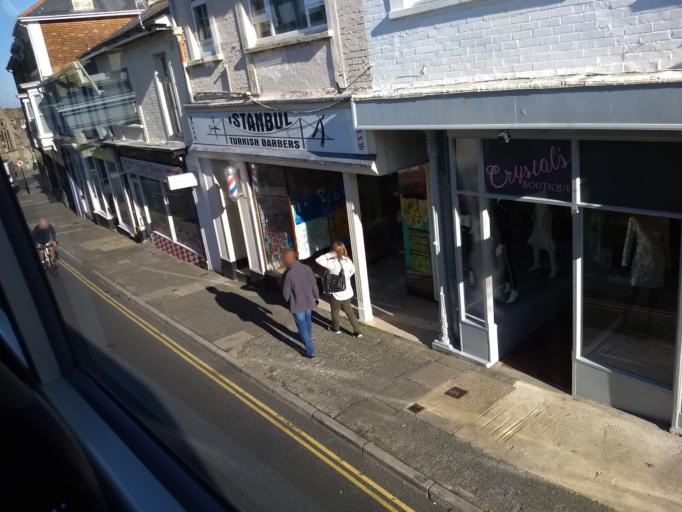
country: GB
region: England
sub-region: Isle of Wight
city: Shanklin
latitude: 50.6288
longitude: -1.1793
